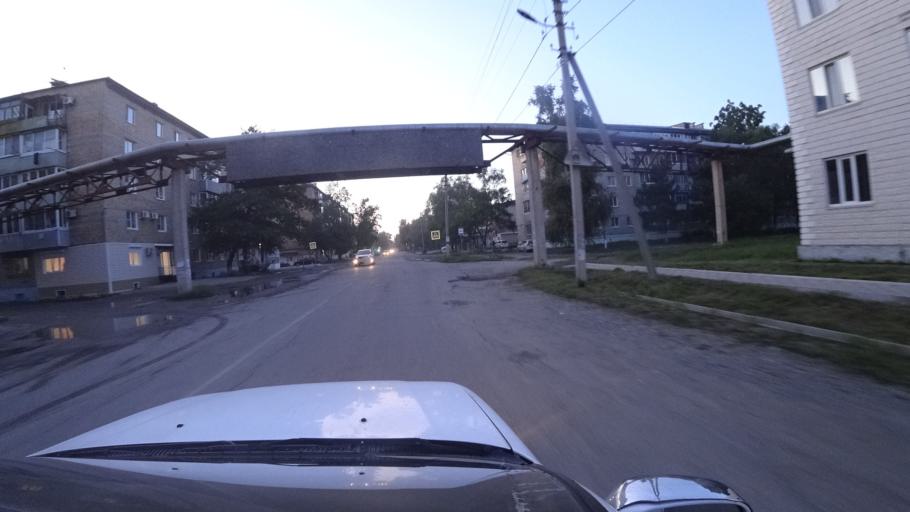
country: RU
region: Primorskiy
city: Dal'nerechensk
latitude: 45.9322
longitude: 133.7361
